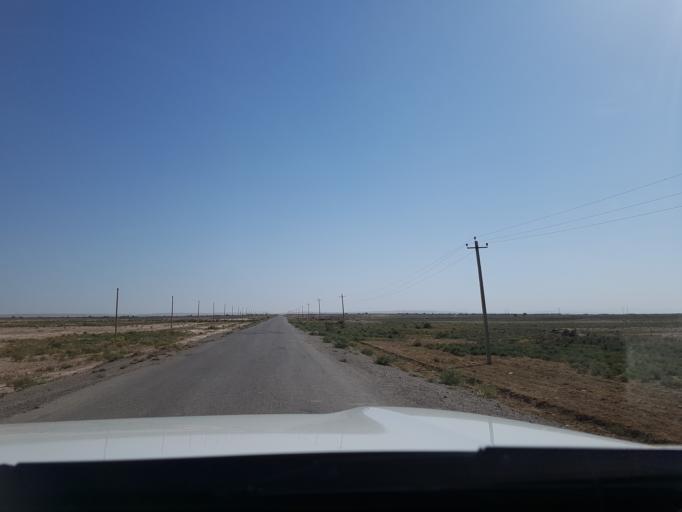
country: IR
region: Razavi Khorasan
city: Sarakhs
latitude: 36.5079
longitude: 61.2533
